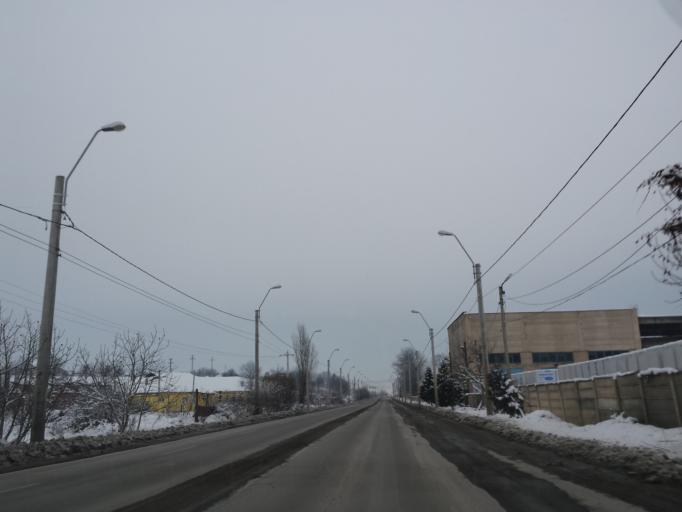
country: RO
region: Hunedoara
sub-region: Municipiul Deva
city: Cristur
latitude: 45.8366
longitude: 22.9473
